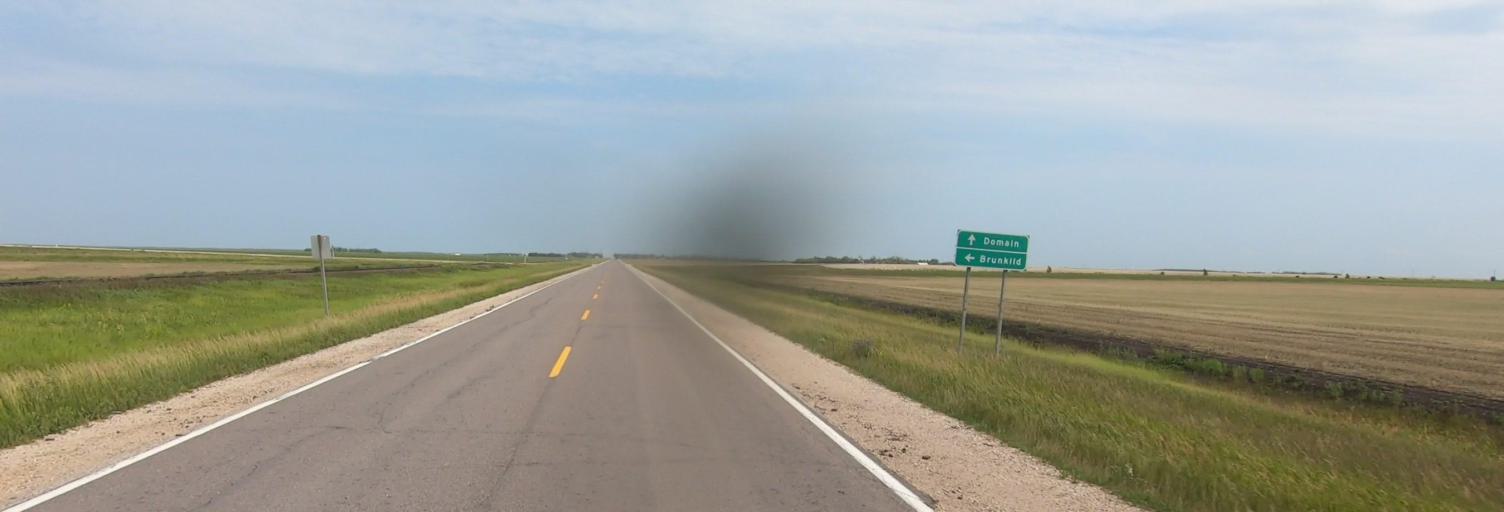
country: CA
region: Manitoba
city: Morris
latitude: 49.5891
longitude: -97.3392
